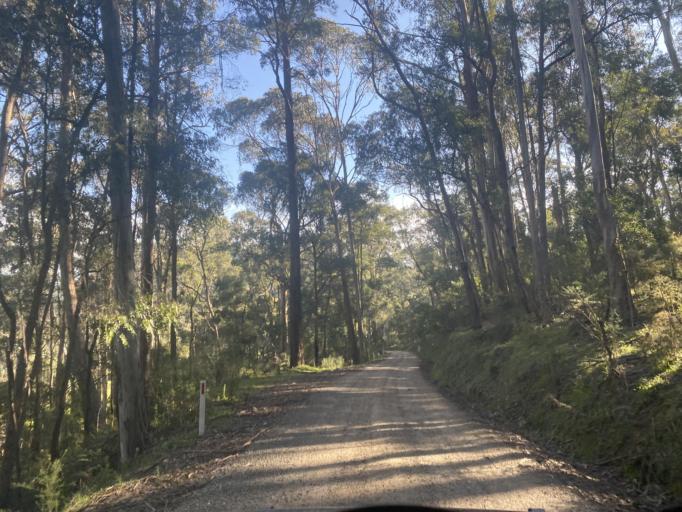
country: AU
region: Victoria
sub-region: Mansfield
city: Mansfield
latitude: -36.8260
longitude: 146.1457
